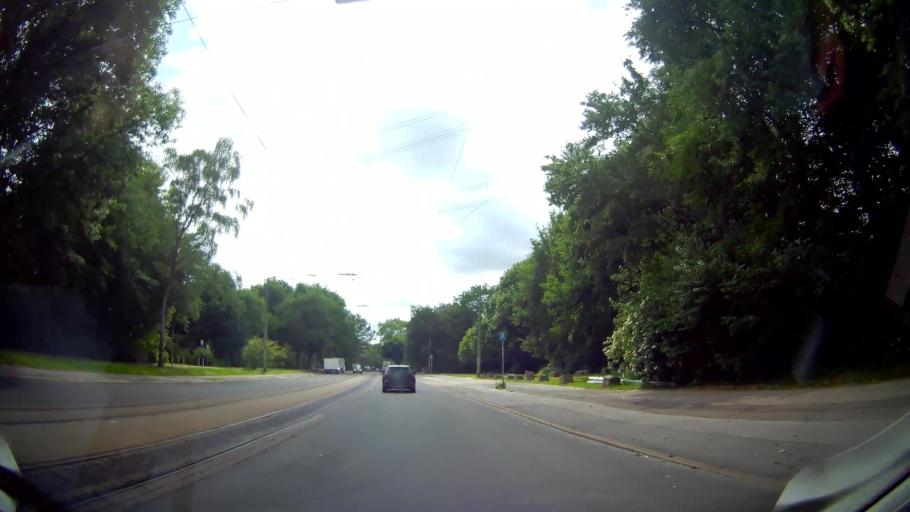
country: DE
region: North Rhine-Westphalia
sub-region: Regierungsbezirk Munster
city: Gelsenkirchen
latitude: 51.5069
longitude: 7.0718
